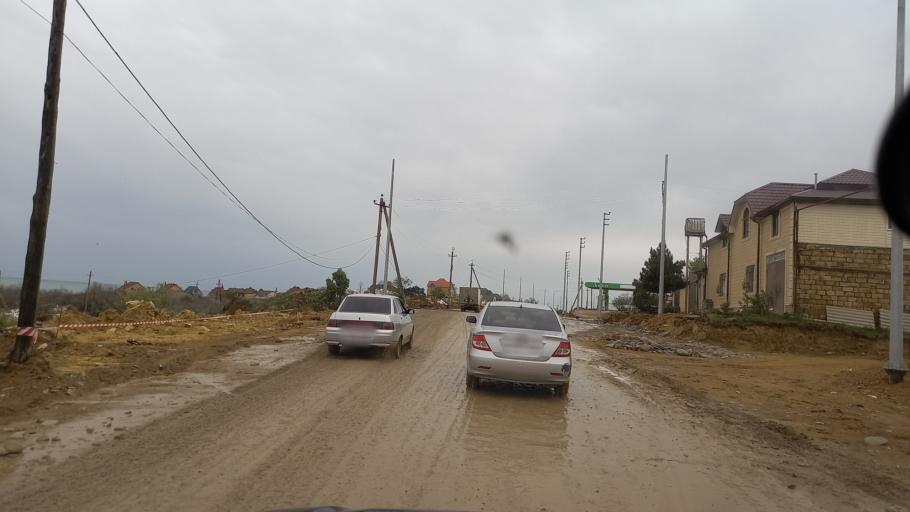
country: RU
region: Dagestan
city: Derbent
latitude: 42.1005
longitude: 48.2846
